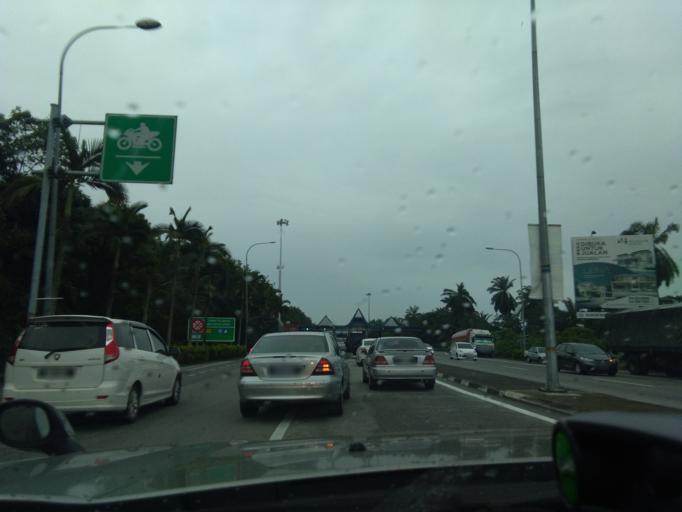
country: MY
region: Penang
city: Nibong Tebal
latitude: 5.1871
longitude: 100.4882
